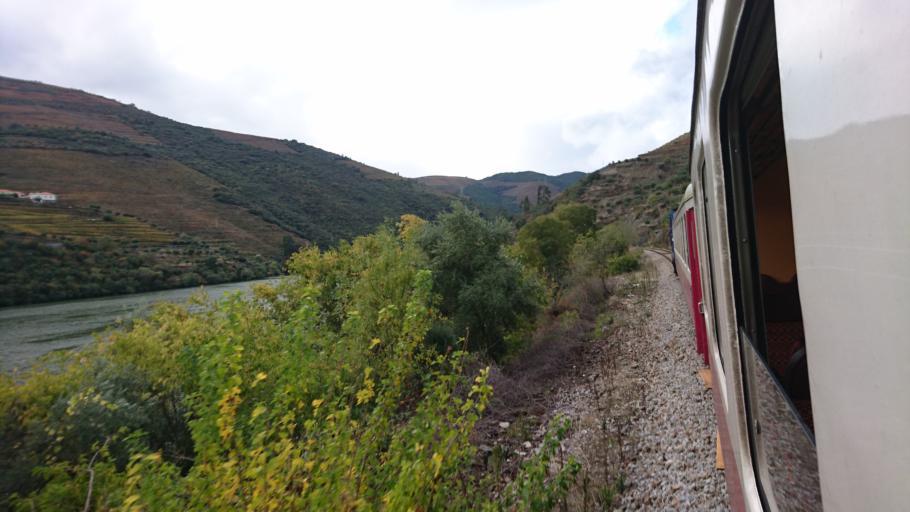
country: PT
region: Viseu
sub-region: Tabuaco
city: Tabuaco
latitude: 41.1666
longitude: -7.5717
